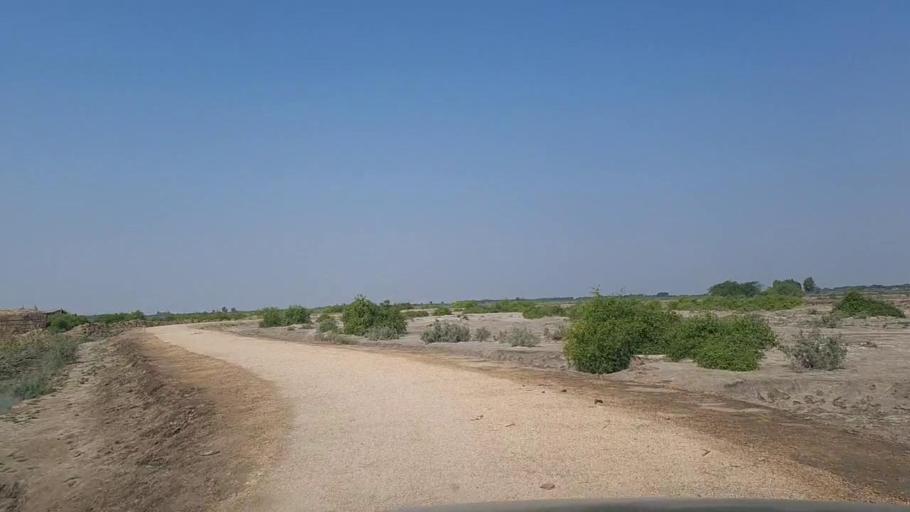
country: PK
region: Sindh
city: Mirpur Sakro
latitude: 24.5068
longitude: 67.7809
